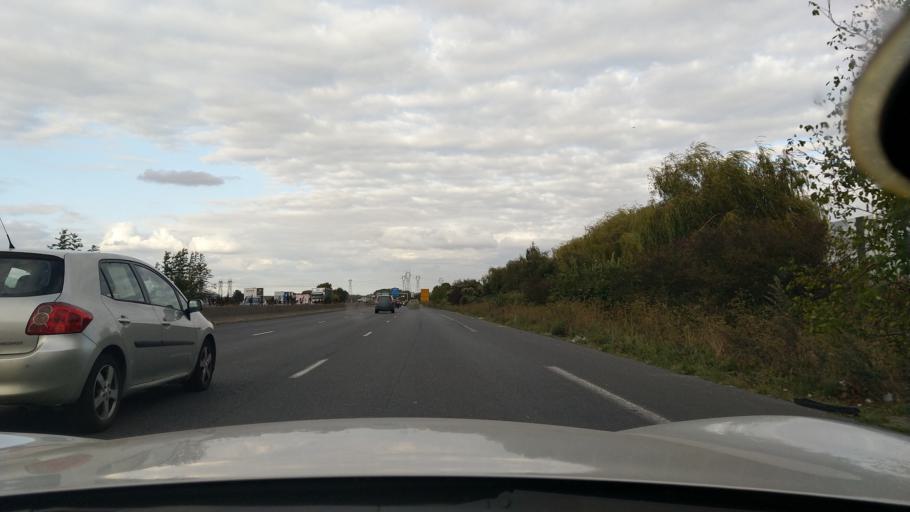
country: FR
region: Ile-de-France
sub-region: Departement de Seine-Saint-Denis
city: Tremblay-en-France
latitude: 48.9690
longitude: 2.5674
